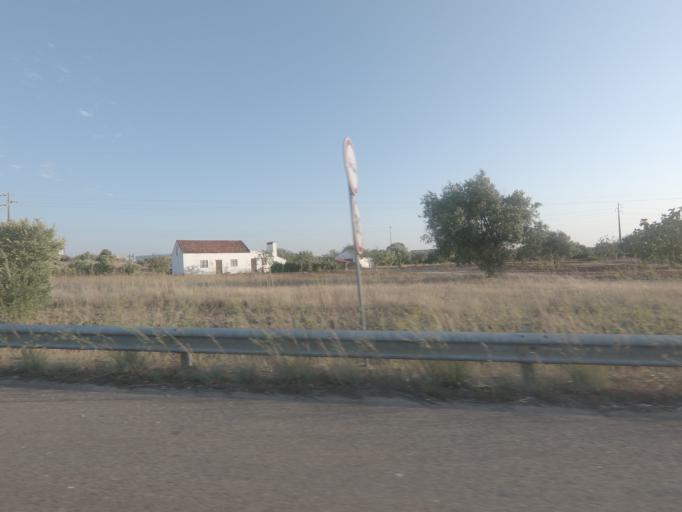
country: PT
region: Santarem
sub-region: Alcanena
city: Alcanena
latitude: 39.4820
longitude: -8.6266
